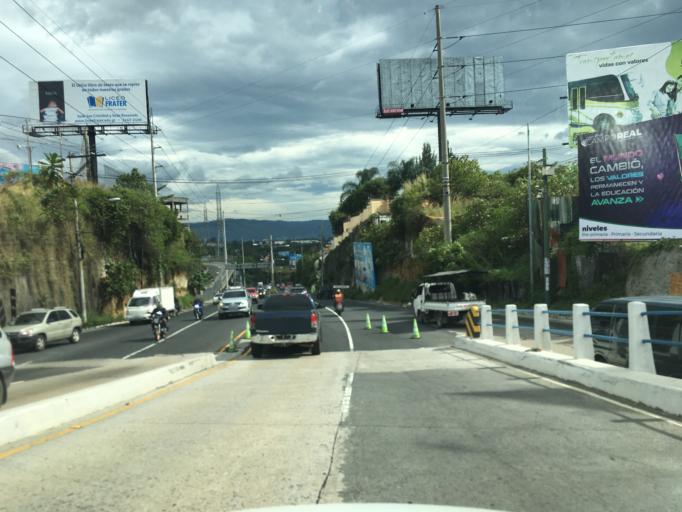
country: GT
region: Guatemala
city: Mixco
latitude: 14.5926
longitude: -90.5786
